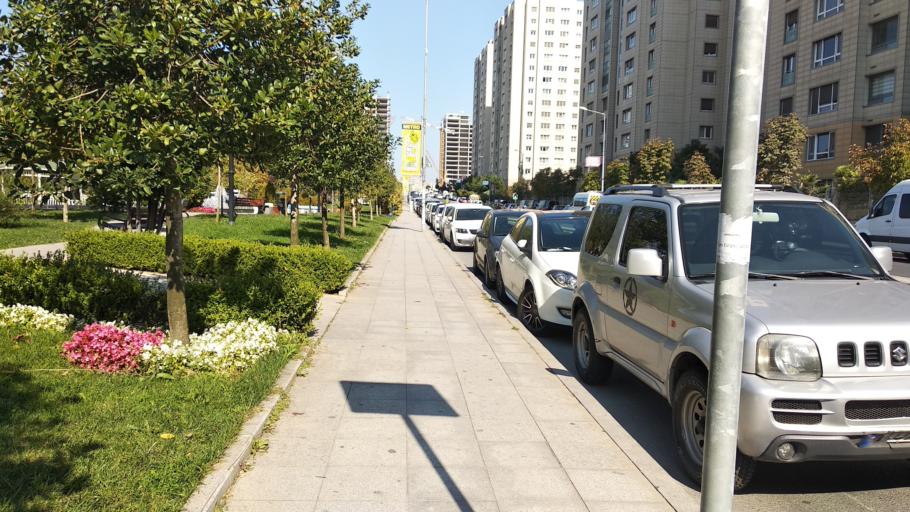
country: TR
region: Istanbul
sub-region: Atasehir
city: Atasehir
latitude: 40.9983
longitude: 29.1027
